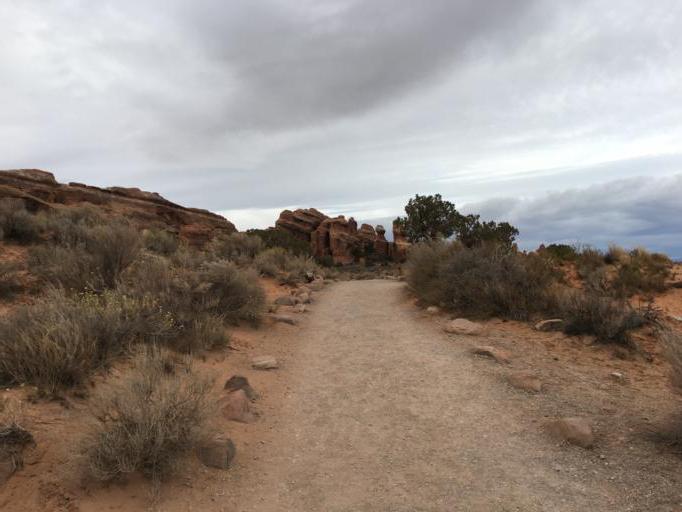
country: US
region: Utah
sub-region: Grand County
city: Moab
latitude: 38.7900
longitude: -109.6027
